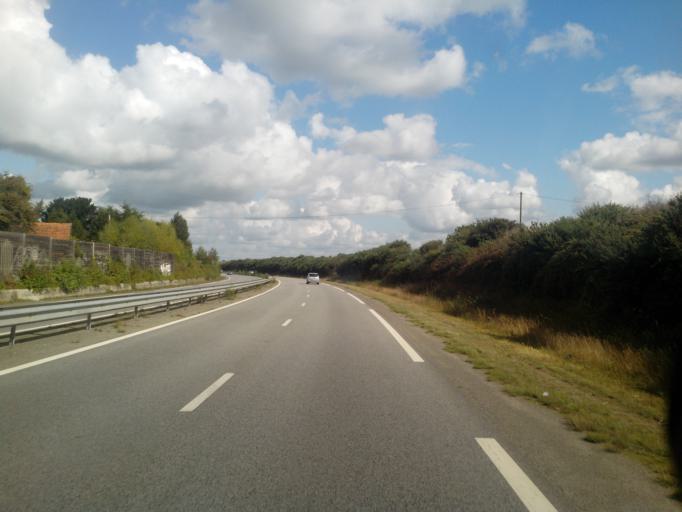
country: FR
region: Brittany
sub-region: Departement d'Ille-et-Vilaine
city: Cesson-Sevigne
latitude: 48.1452
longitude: -1.6250
